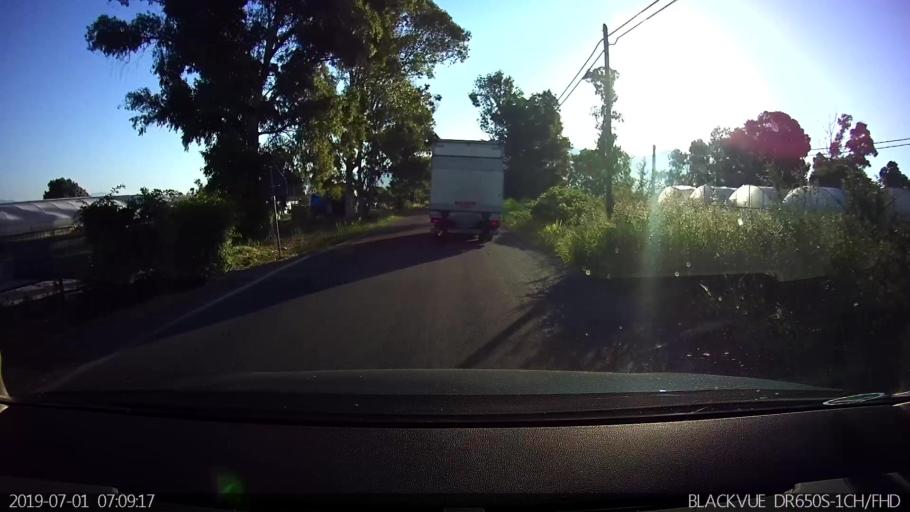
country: IT
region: Latium
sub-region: Provincia di Latina
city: Borgo Hermada
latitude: 41.3041
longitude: 13.1593
